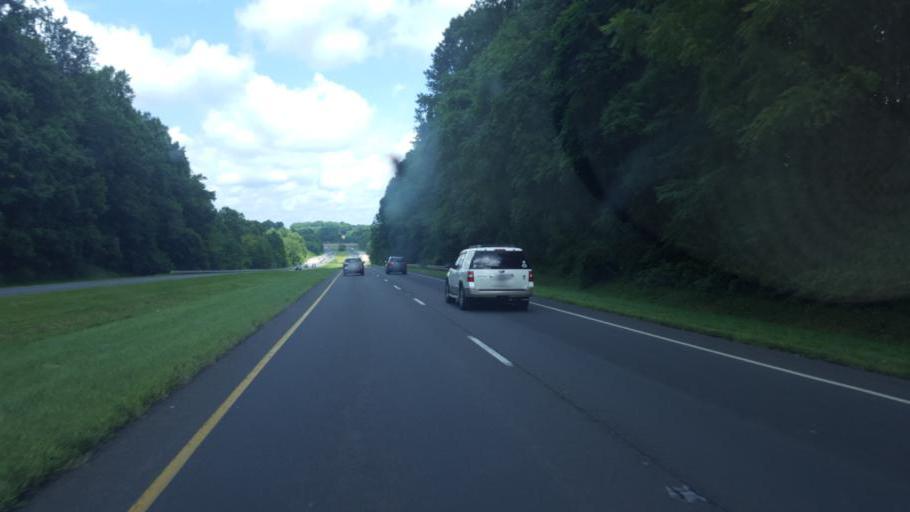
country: US
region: Virginia
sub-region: Fauquier County
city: Warrenton
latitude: 38.6900
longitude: -77.7854
